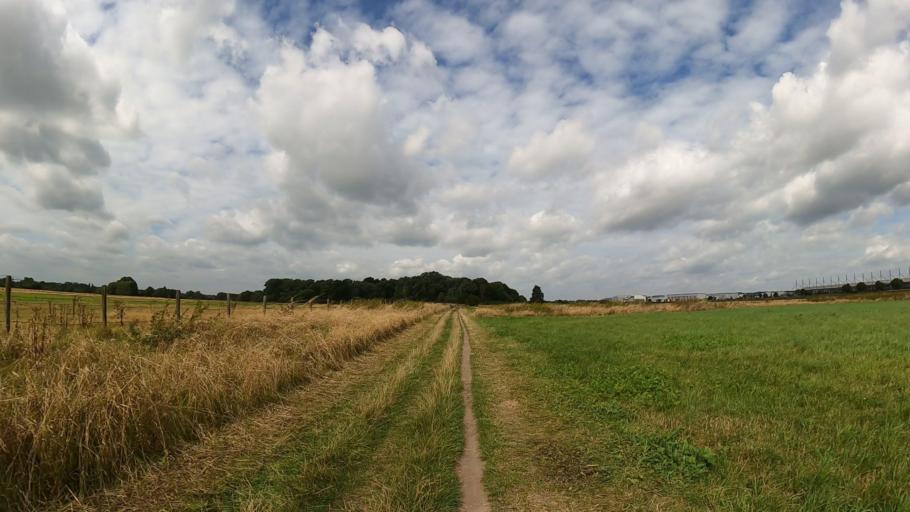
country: DE
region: Lower Saxony
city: Neu Wulmstorf
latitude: 53.5275
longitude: 9.8363
